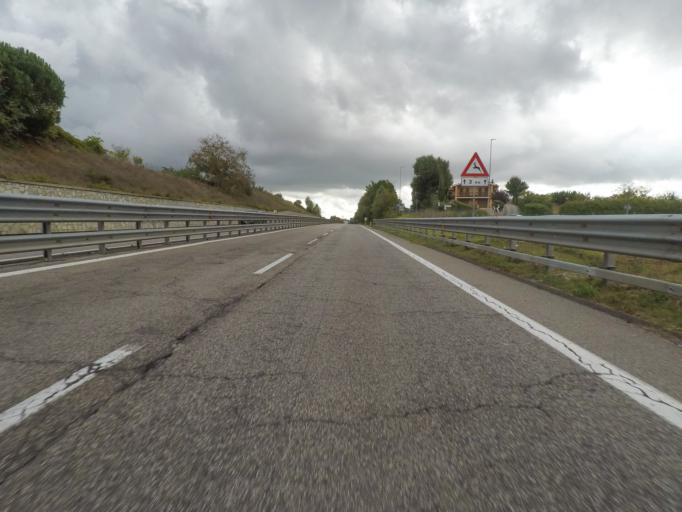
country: IT
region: Tuscany
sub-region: Provincia di Siena
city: Taverne D'Arbia
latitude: 43.2980
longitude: 11.3882
